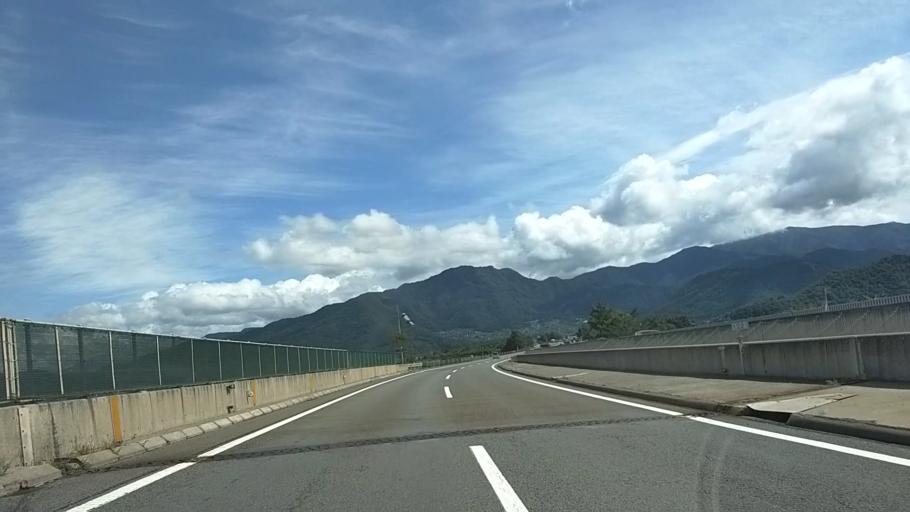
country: JP
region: Nagano
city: Nagano-shi
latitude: 36.5639
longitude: 138.1736
